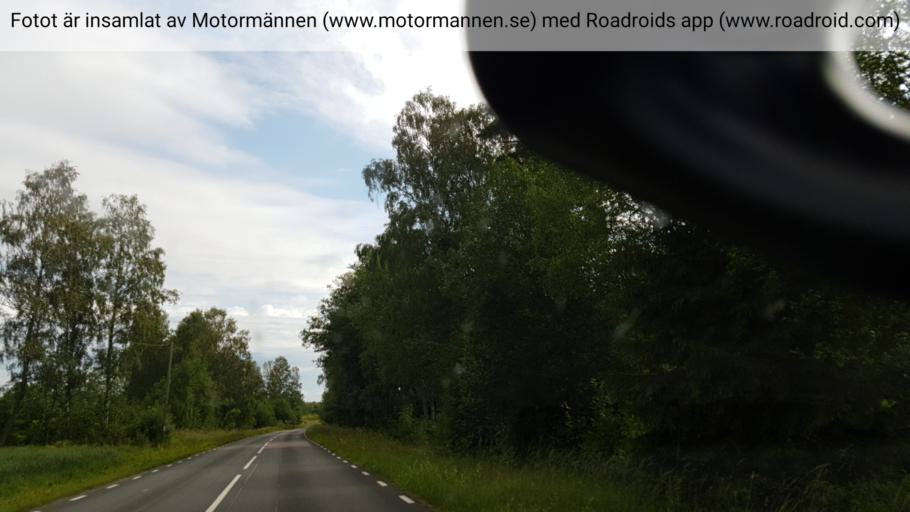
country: SE
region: Vaestra Goetaland
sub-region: Falkopings Kommun
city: Floby
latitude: 58.2076
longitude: 13.3706
